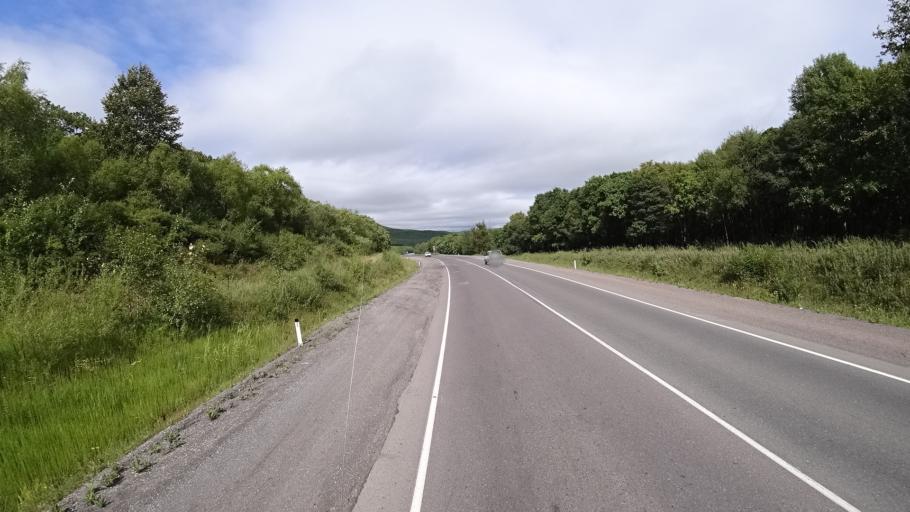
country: RU
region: Primorskiy
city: Lyalichi
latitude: 44.1308
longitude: 132.4270
